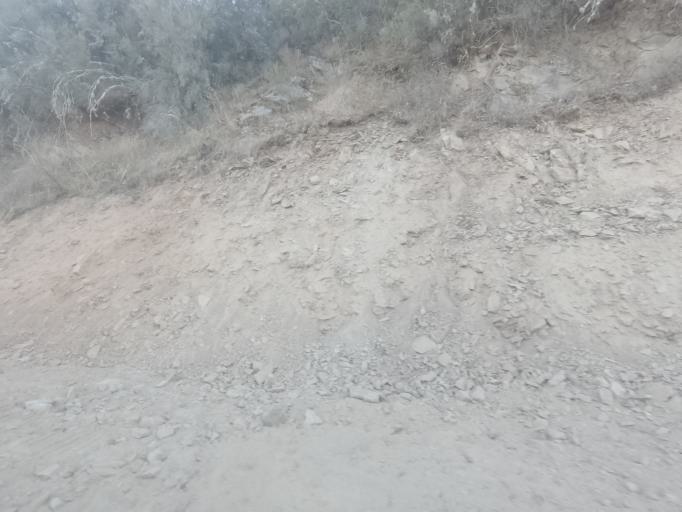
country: PT
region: Viseu
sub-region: Armamar
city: Armamar
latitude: 41.1543
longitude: -7.6441
